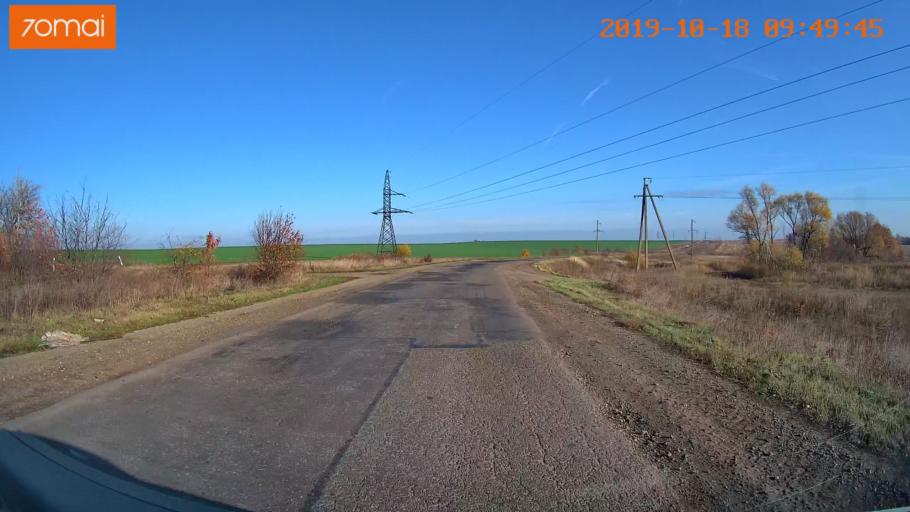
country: RU
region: Tula
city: Kazachka
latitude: 53.3214
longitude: 38.2690
